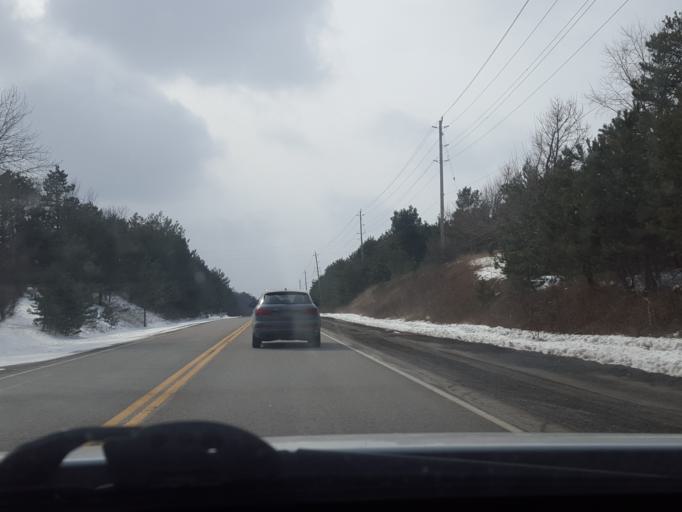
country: CA
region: Ontario
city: Uxbridge
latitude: 44.0425
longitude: -79.1606
